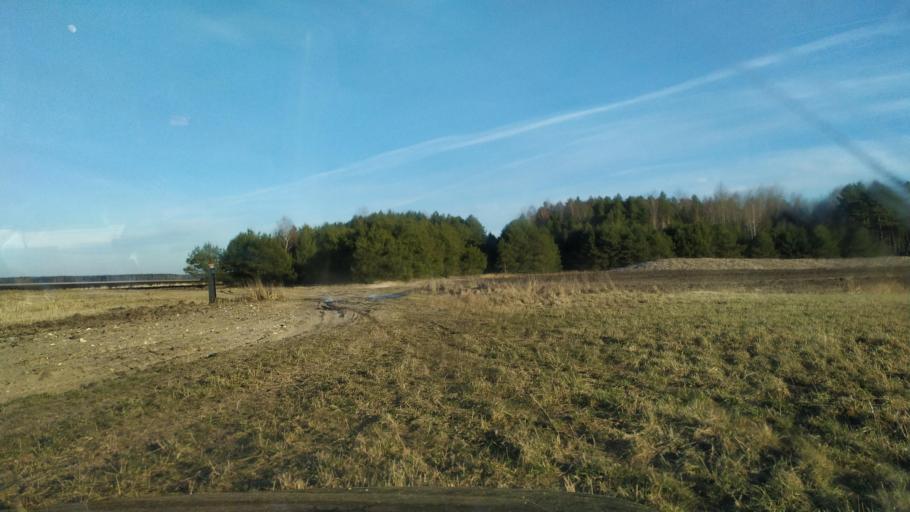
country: BY
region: Brest
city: Pruzhany
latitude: 52.5445
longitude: 24.3032
